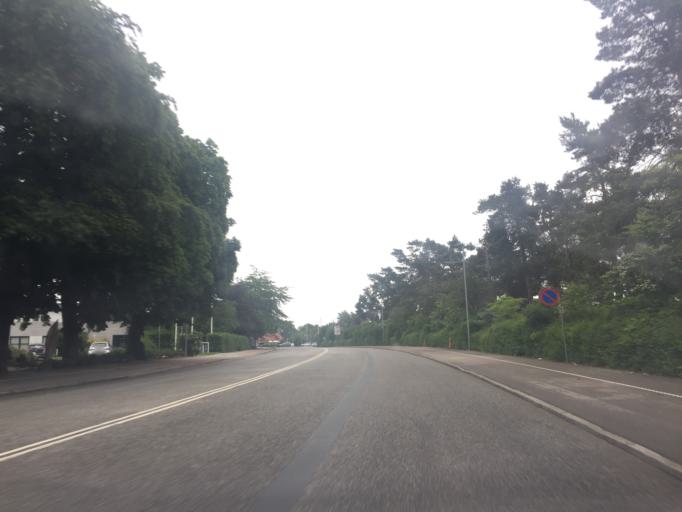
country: DK
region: Capital Region
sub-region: Glostrup Kommune
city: Glostrup
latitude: 55.6753
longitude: 12.3916
